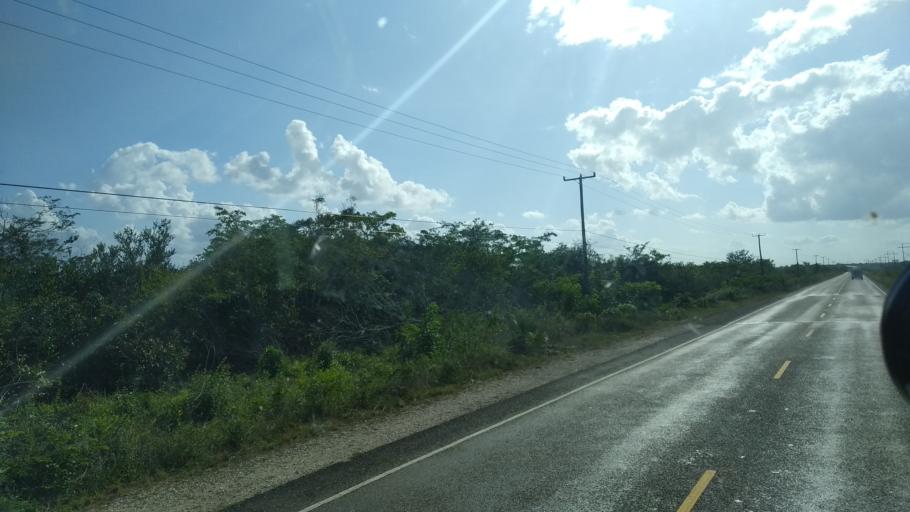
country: BZ
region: Belize
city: Belize City
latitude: 17.4060
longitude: -88.4855
